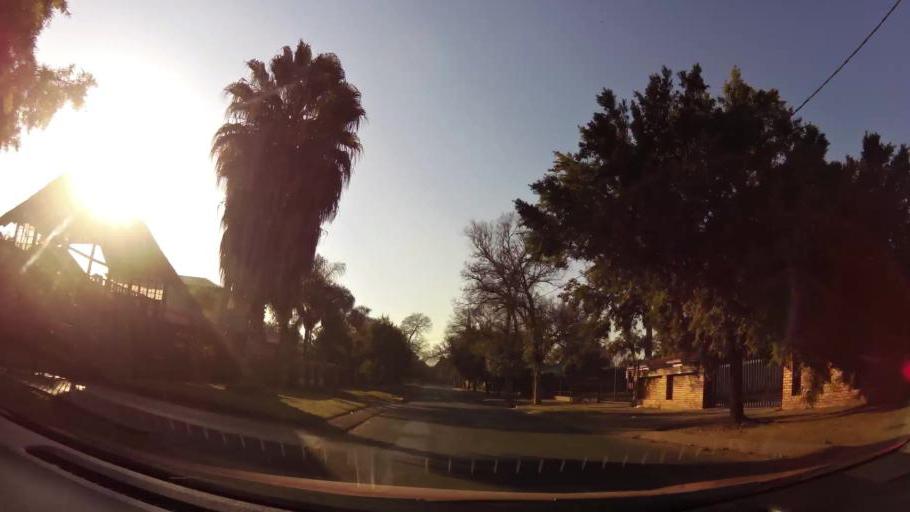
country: ZA
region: Gauteng
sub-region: City of Tshwane Metropolitan Municipality
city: Pretoria
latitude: -25.7042
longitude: 28.1806
